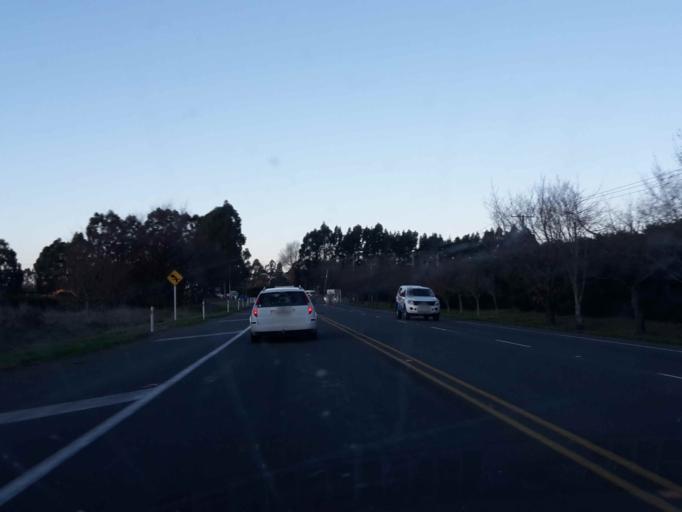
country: NZ
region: Canterbury
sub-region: Selwyn District
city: Rolleston
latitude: -43.5825
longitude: 172.4071
